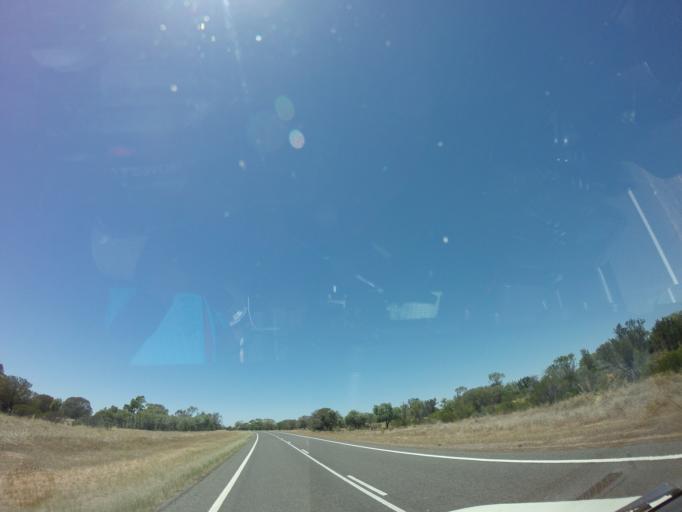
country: AU
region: New South Wales
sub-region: Cobar
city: Cobar
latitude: -31.5752
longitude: 144.7993
